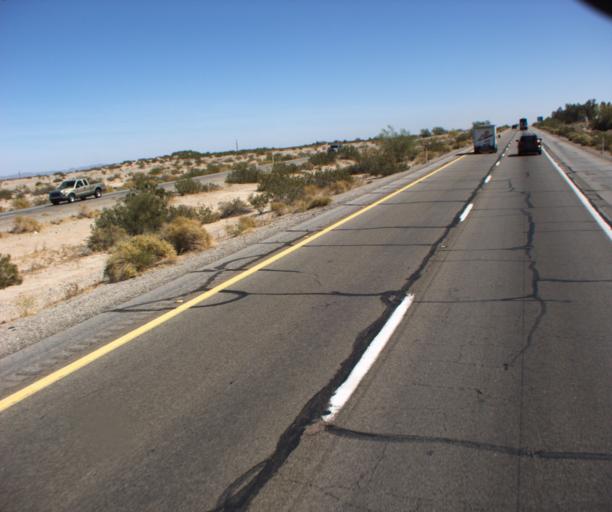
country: US
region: Arizona
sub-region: Yuma County
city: Wellton
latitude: 32.6536
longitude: -114.1767
